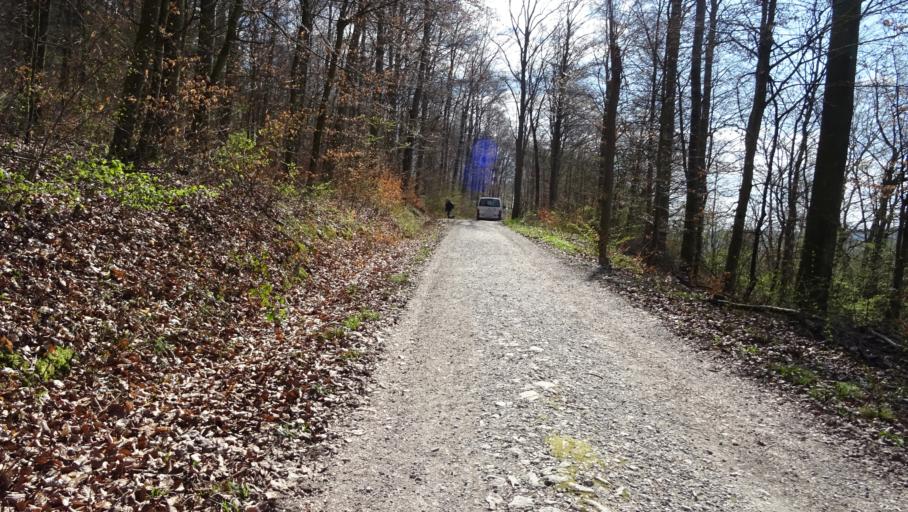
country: DE
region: Baden-Wuerttemberg
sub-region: Karlsruhe Region
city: Neckarzimmern
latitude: 49.3345
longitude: 9.1246
